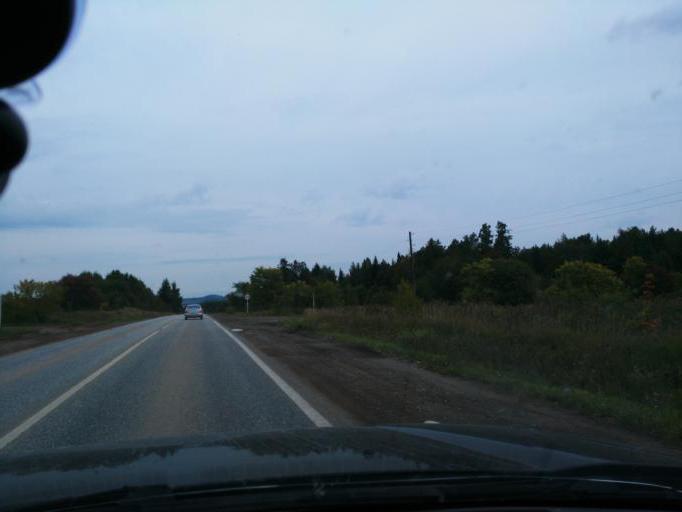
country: RU
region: Perm
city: Chernushka
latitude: 56.5861
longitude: 56.1477
